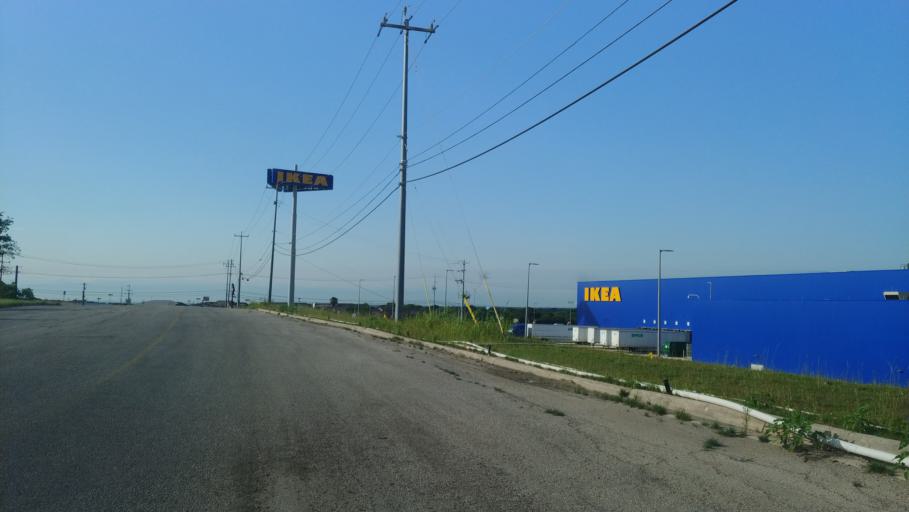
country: US
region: Texas
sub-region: Bexar County
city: Live Oak
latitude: 29.5677
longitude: -98.3372
